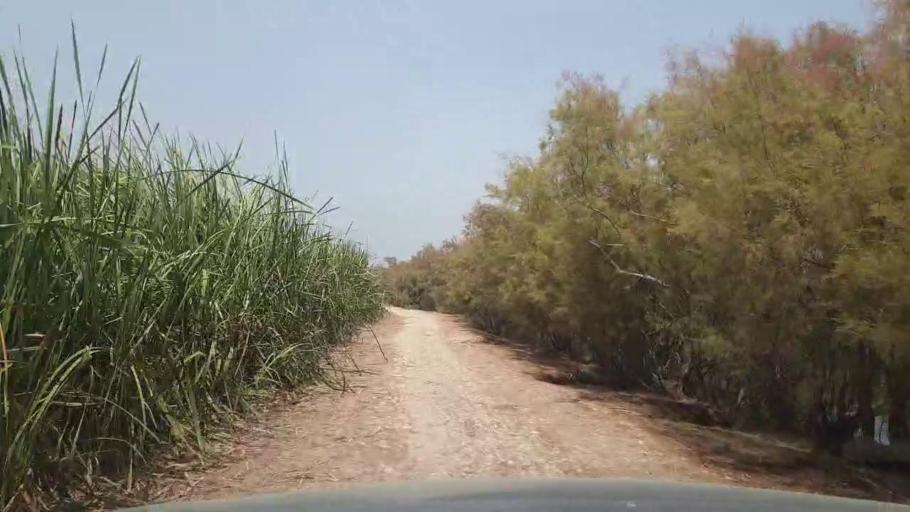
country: PK
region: Sindh
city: Garhi Yasin
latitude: 27.9510
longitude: 68.4363
